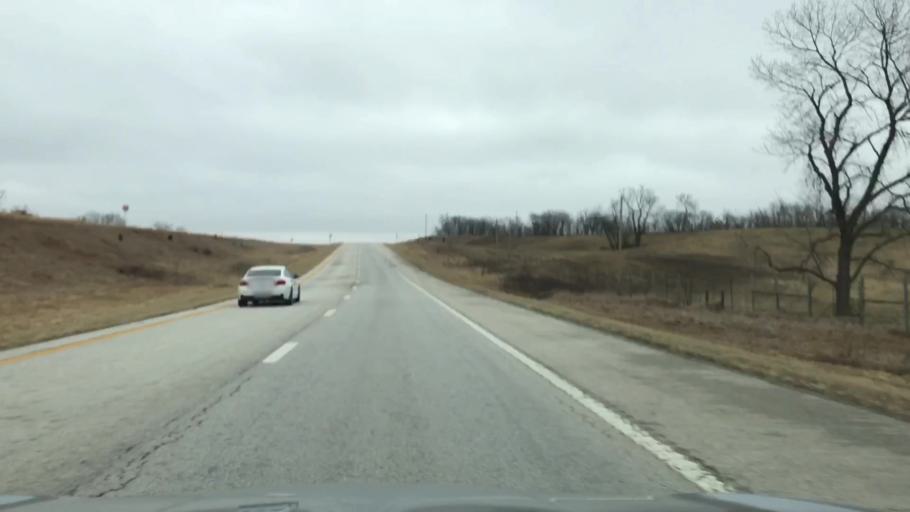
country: US
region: Missouri
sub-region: Linn County
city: Marceline
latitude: 39.7590
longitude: -92.8744
